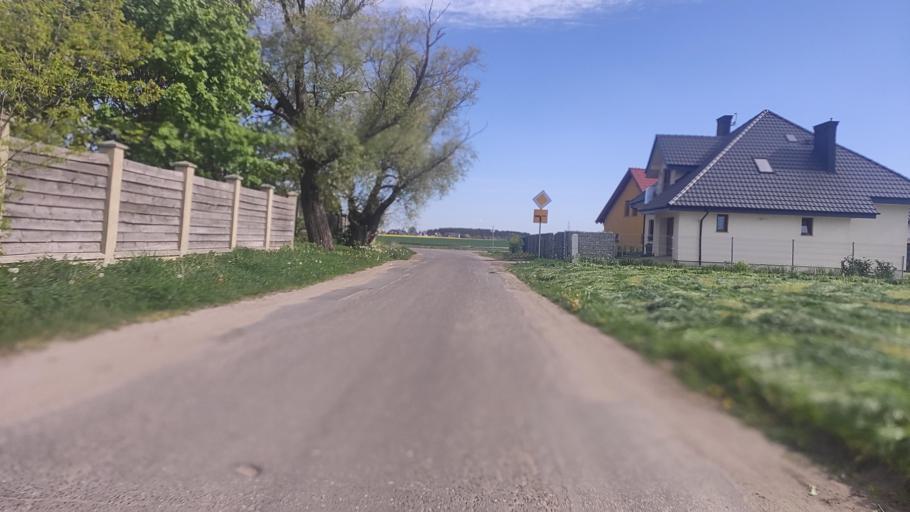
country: PL
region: Greater Poland Voivodeship
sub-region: Powiat poznanski
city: Kleszczewo
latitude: 52.3849
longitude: 17.1442
